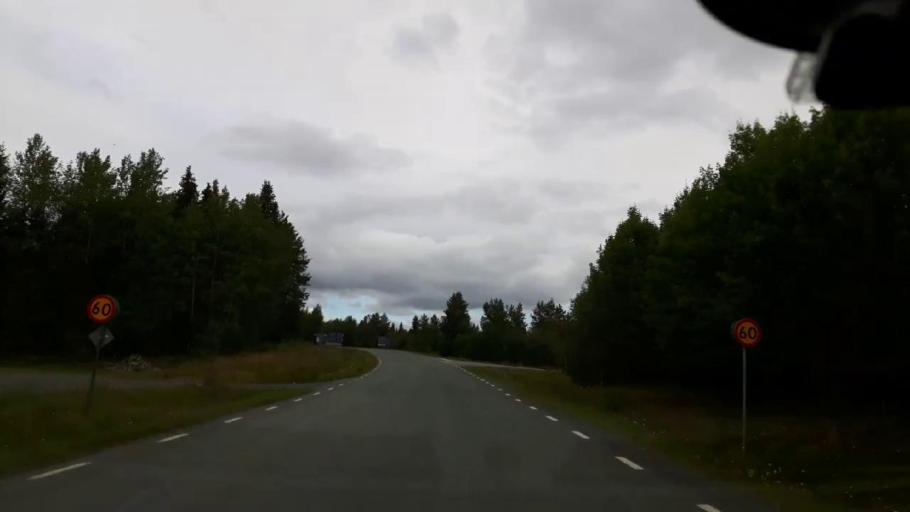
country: SE
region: Jaemtland
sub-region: Krokoms Kommun
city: Valla
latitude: 63.5687
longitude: 13.8408
